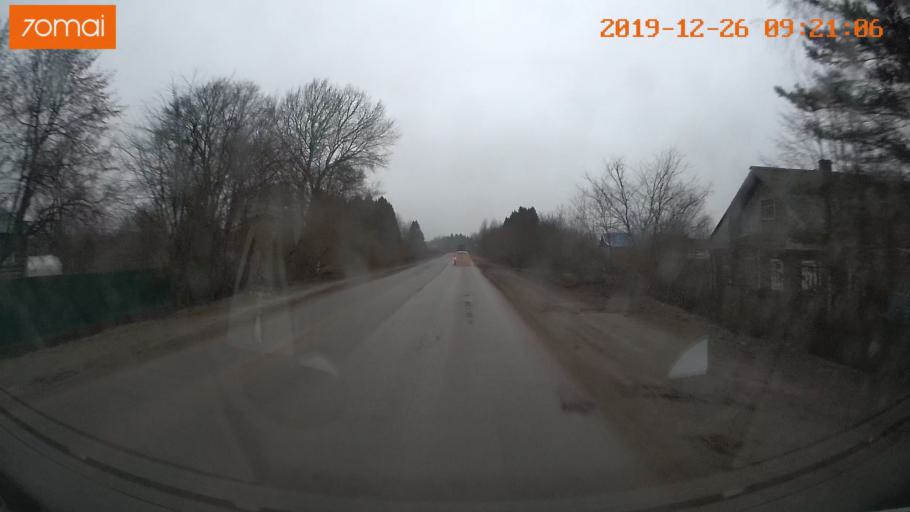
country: RU
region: Vologda
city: Gryazovets
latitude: 58.9674
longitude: 40.2263
